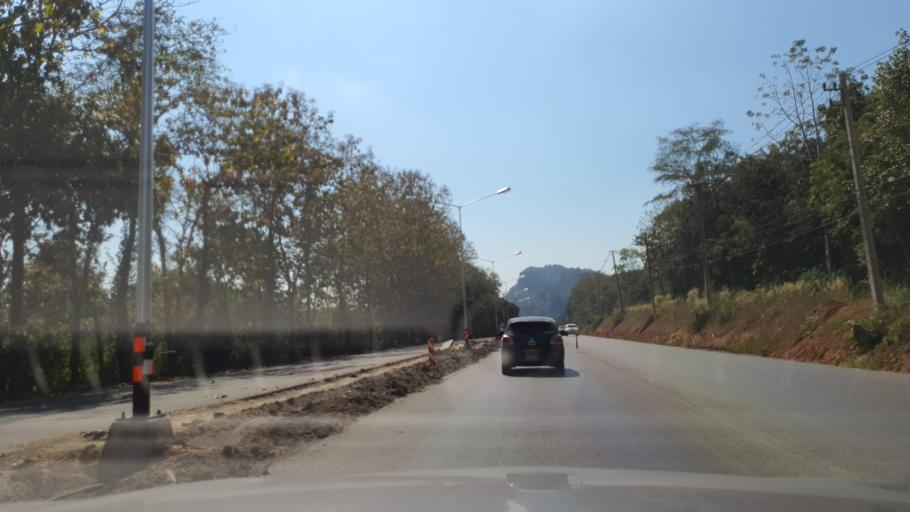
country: TH
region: Nan
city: Nan
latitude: 18.8719
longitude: 100.7429
